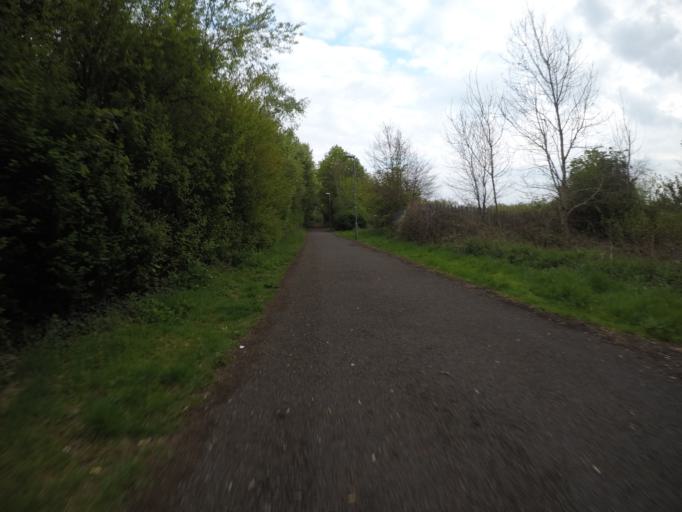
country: GB
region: Scotland
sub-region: North Ayrshire
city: Irvine
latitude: 55.6339
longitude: -4.6300
